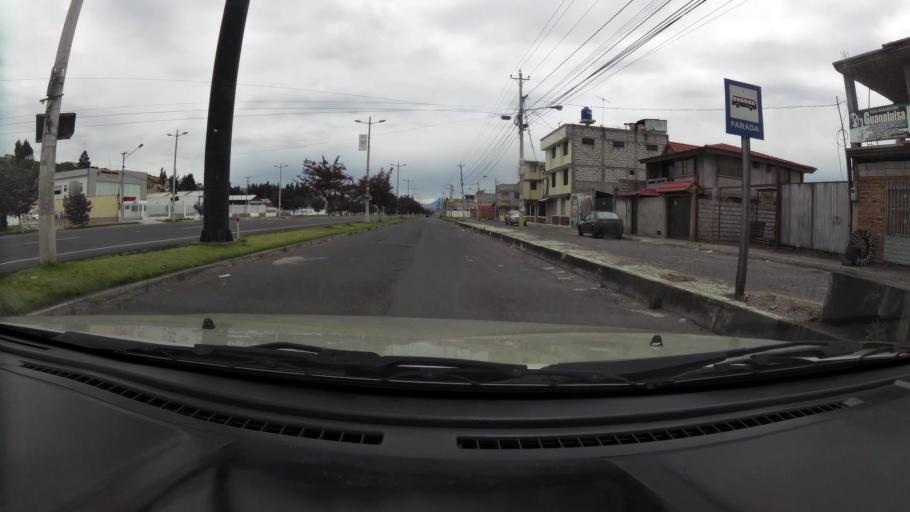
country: EC
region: Cotopaxi
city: Latacunga
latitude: -0.9633
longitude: -78.6111
